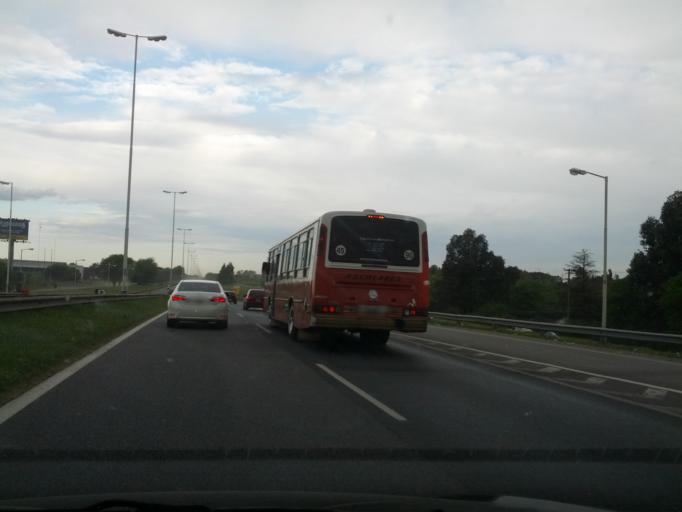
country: AR
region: Buenos Aires
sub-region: Partido de General Rodriguez
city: General Rodriguez
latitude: -34.5828
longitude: -58.9957
